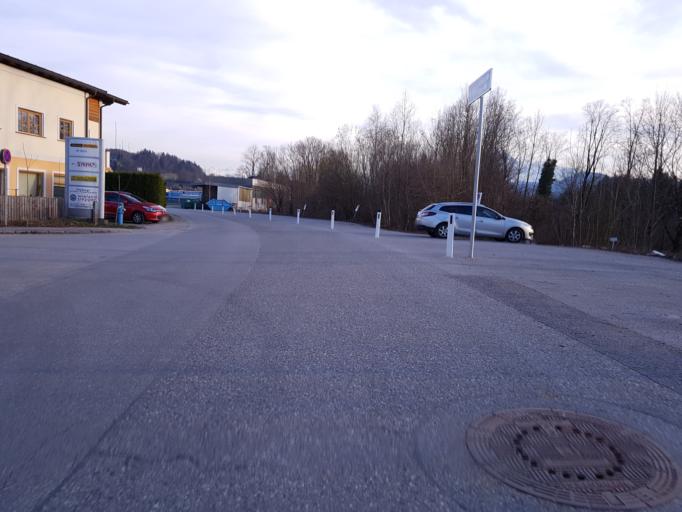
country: AT
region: Salzburg
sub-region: Politischer Bezirk Salzburg-Umgebung
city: Elsbethen
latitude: 47.7511
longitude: 13.0809
